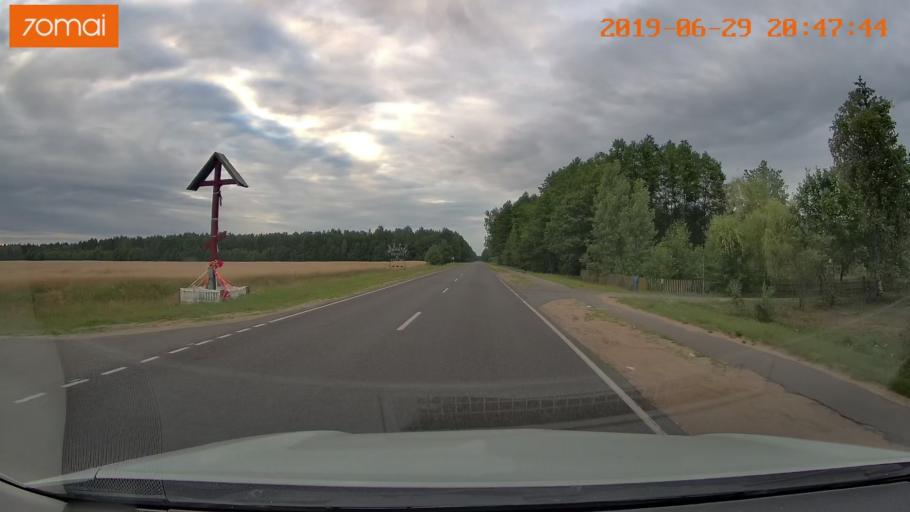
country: BY
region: Brest
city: Hantsavichy
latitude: 52.6417
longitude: 26.3161
